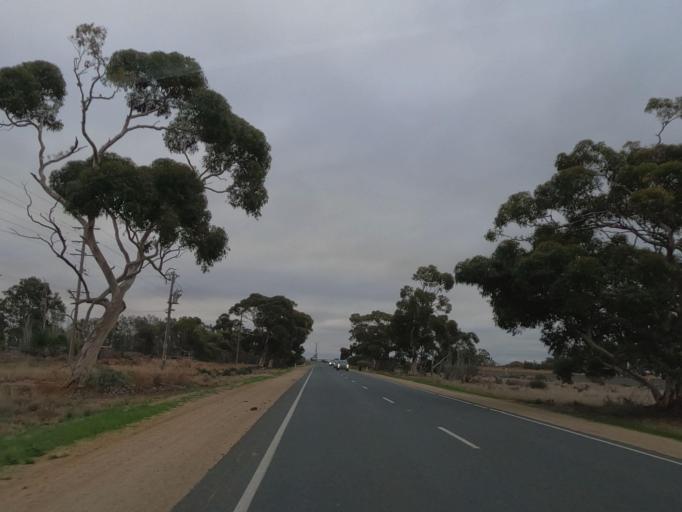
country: AU
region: Victoria
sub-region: Swan Hill
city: Swan Hill
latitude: -35.3975
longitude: 143.5745
